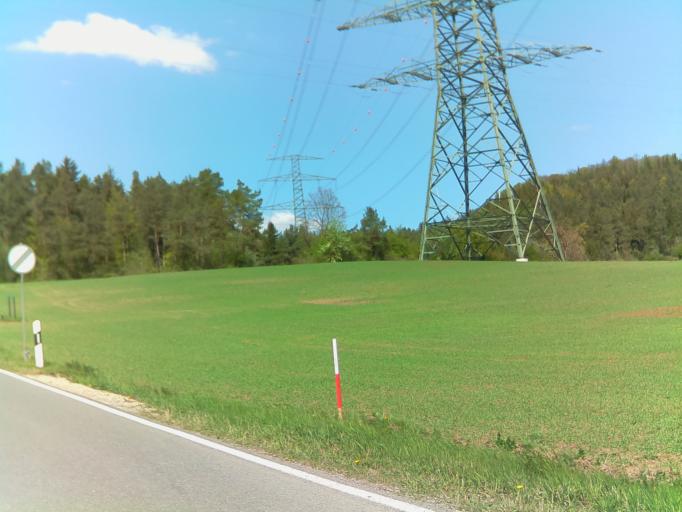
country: DE
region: Thuringia
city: Behringen
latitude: 50.7532
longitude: 11.0087
